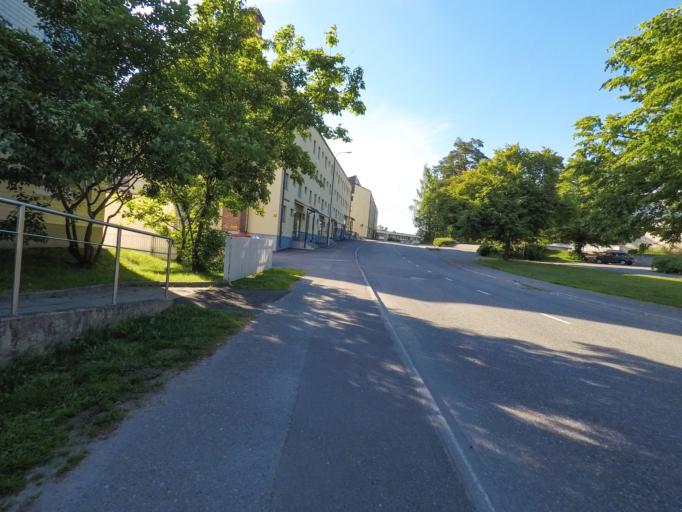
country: FI
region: Southern Savonia
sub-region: Savonlinna
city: Savonlinna
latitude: 61.8641
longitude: 28.8574
